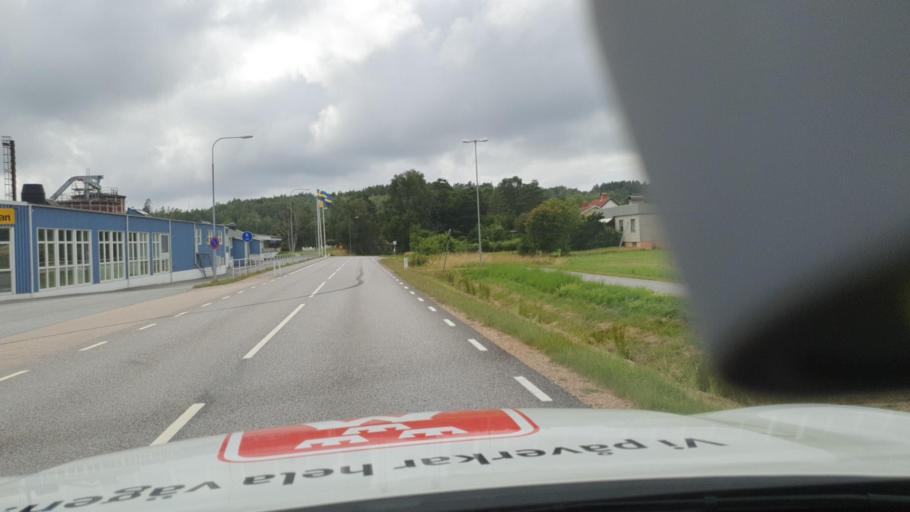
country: SE
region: Vaestra Goetaland
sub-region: Tanums Kommun
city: Tanumshede
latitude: 58.7199
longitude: 11.2981
